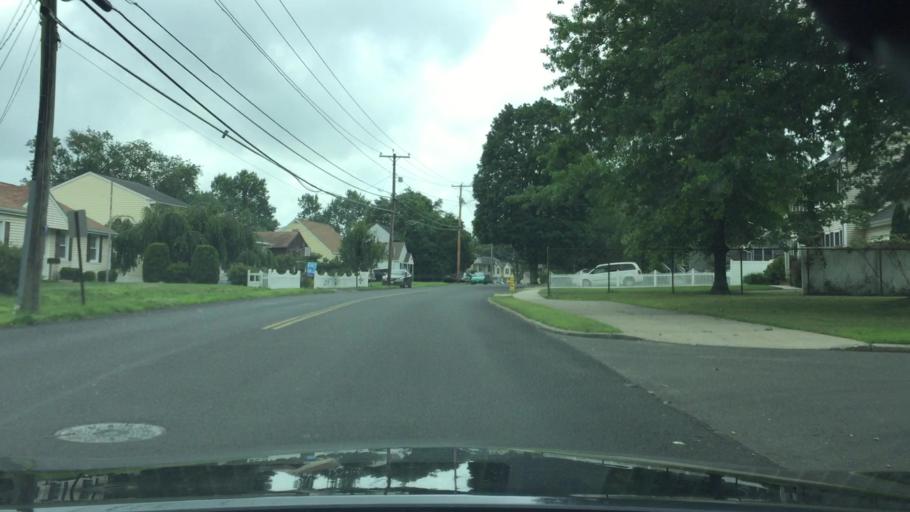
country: US
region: Connecticut
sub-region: New Haven County
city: City of Milford (balance)
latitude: 41.2027
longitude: -73.0874
